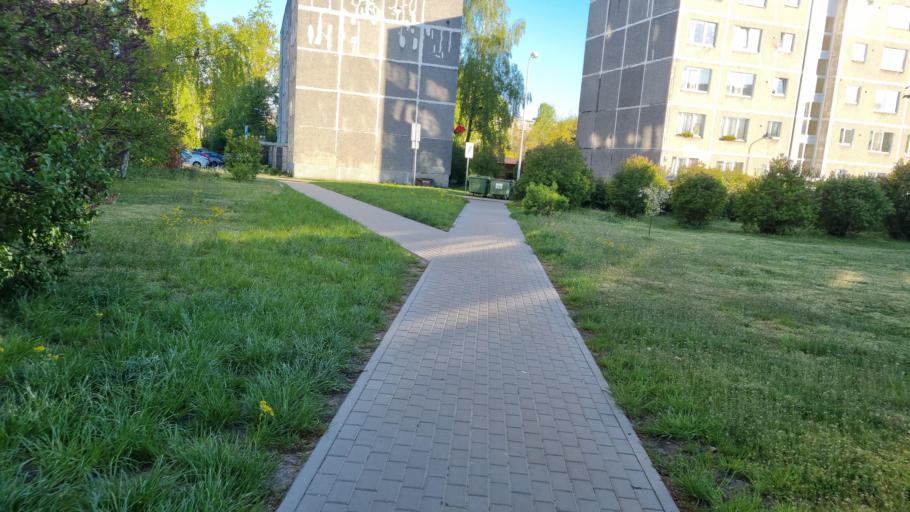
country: LV
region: Riga
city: Bolderaja
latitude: 57.0329
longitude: 24.0537
